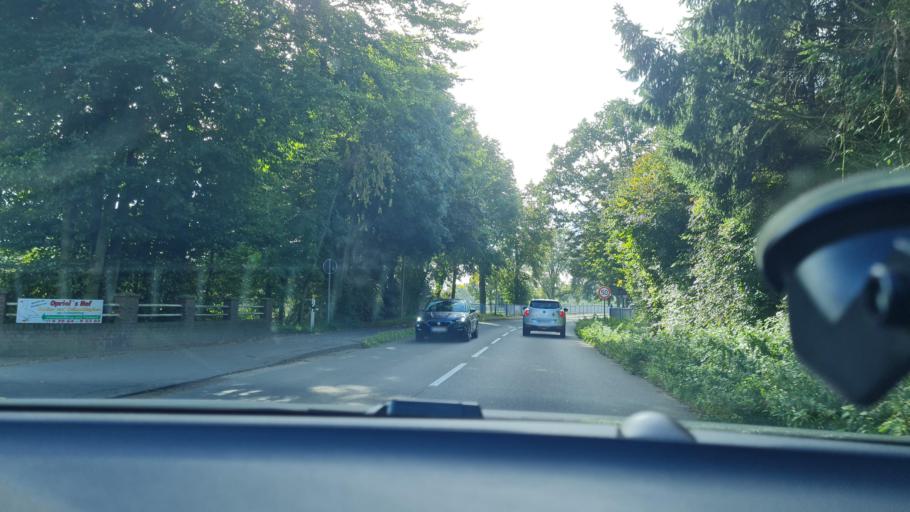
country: DE
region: North Rhine-Westphalia
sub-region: Regierungsbezirk Dusseldorf
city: Dinslaken
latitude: 51.5415
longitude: 6.7714
